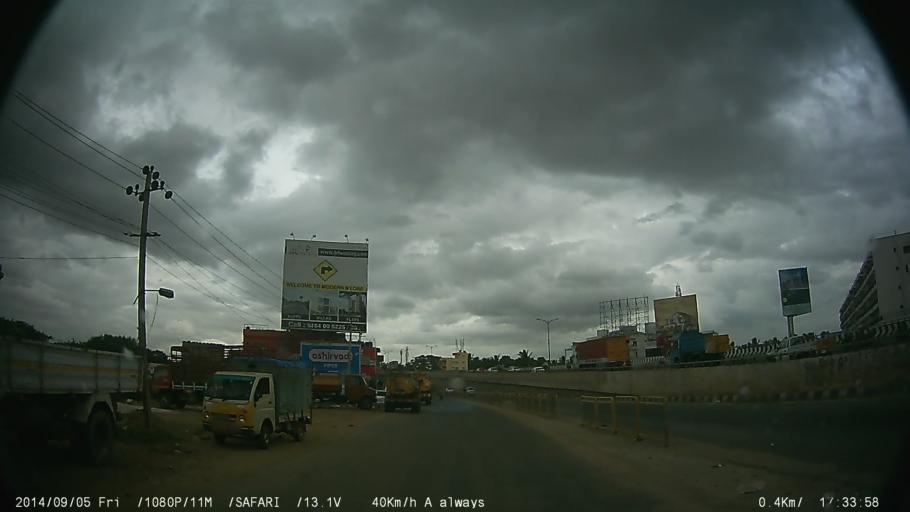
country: IN
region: Karnataka
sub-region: Bangalore Urban
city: Anekal
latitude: 12.8041
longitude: 77.7012
